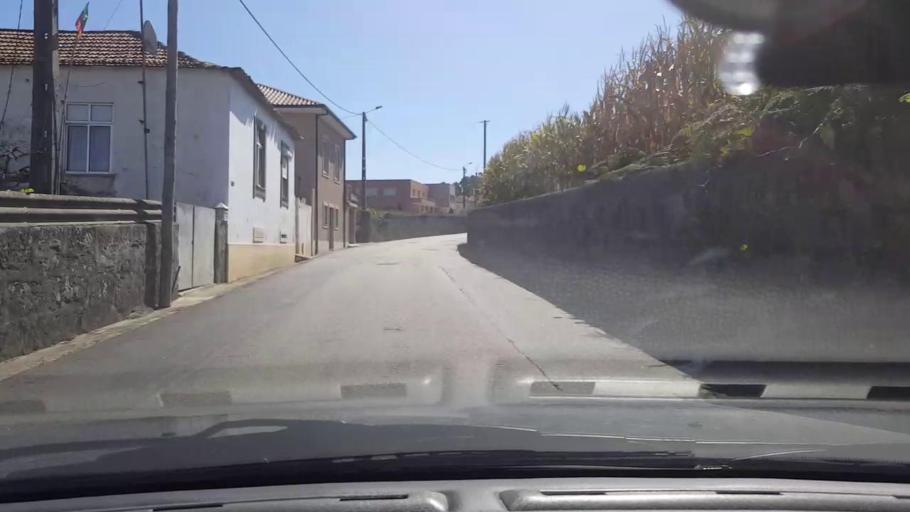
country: PT
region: Porto
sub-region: Matosinhos
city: Lavra
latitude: 41.2648
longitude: -8.6906
